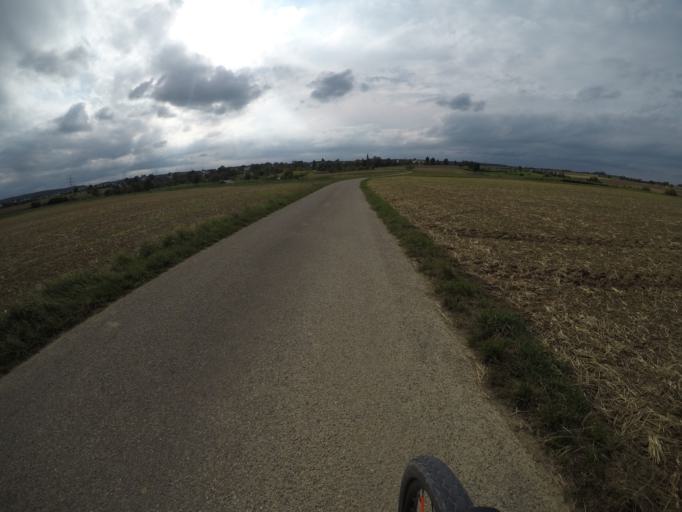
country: DE
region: Baden-Wuerttemberg
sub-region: Regierungsbezirk Stuttgart
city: Deckenpfronn
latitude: 48.6247
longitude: 8.8469
